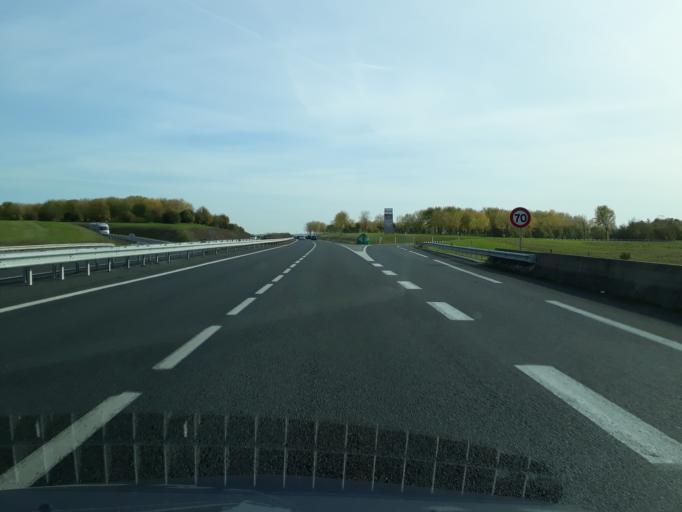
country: FR
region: Bourgogne
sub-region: Departement de l'Yonne
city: Thorigny-sur-Oreuse
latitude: 48.2460
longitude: 3.5482
